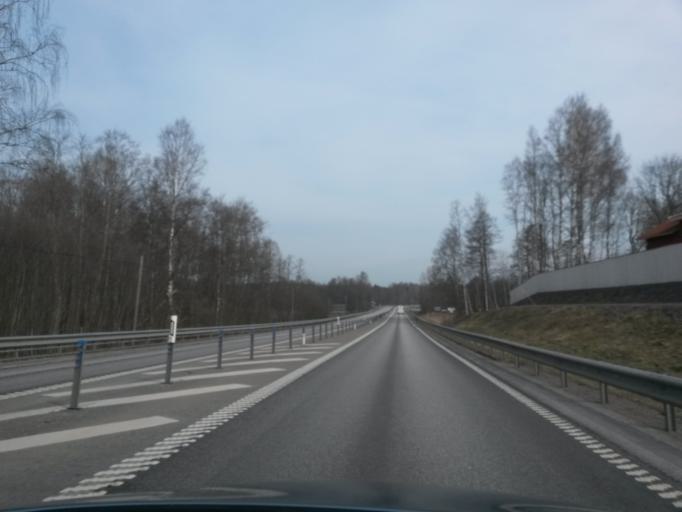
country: SE
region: OErebro
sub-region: Laxa Kommun
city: Laxa
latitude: 58.9668
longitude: 14.5371
